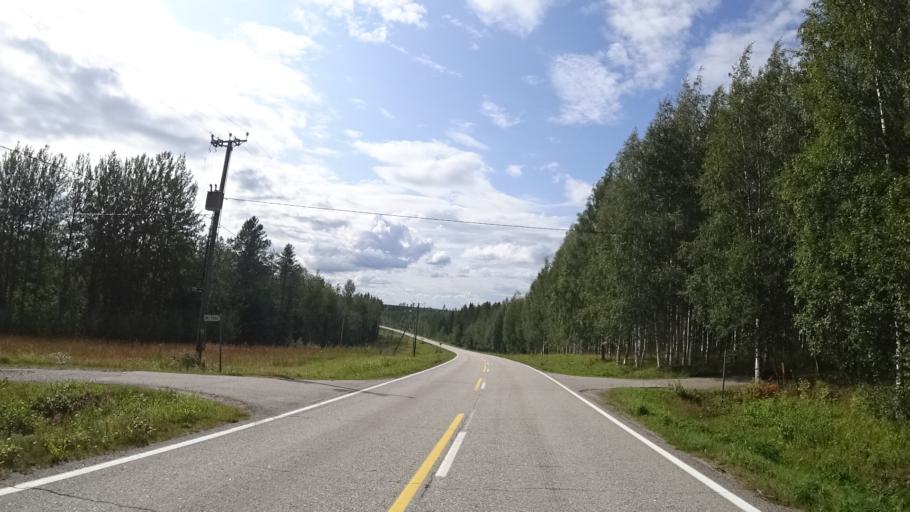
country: FI
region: North Karelia
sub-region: Joensuu
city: Ilomantsi
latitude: 62.7968
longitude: 31.1193
